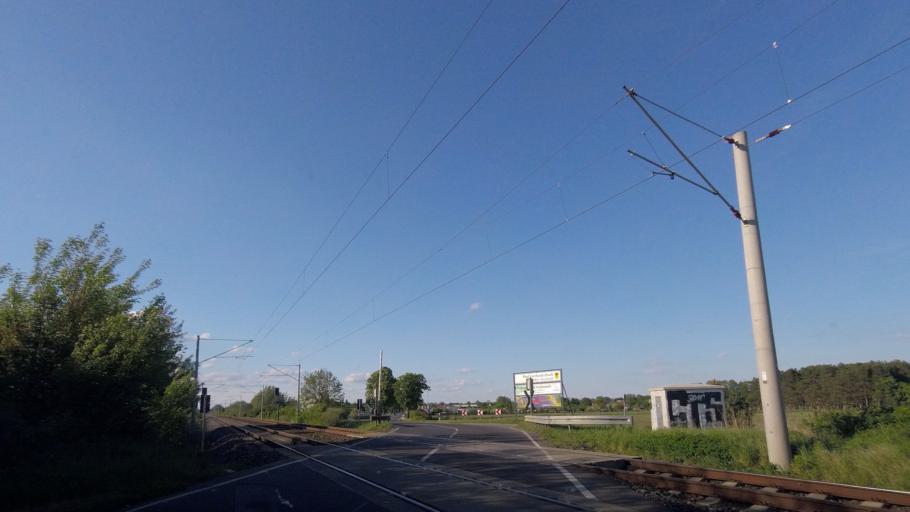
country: DE
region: Brandenburg
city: Luebben
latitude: 51.9194
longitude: 13.8953
